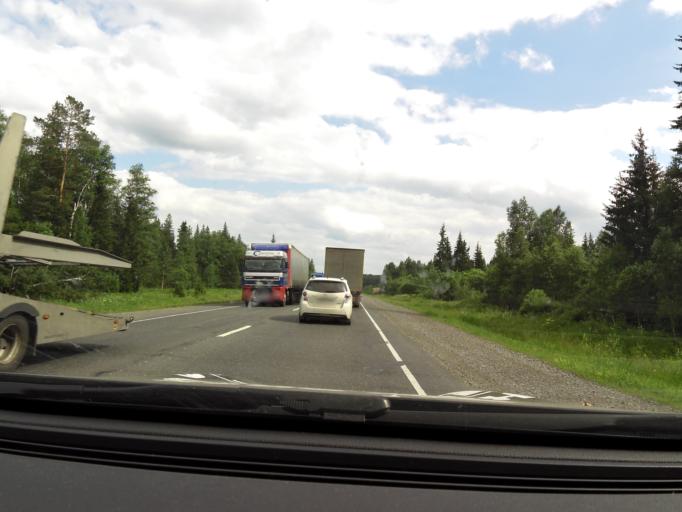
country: RU
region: Sverdlovsk
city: Atig
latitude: 56.8086
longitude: 59.3672
